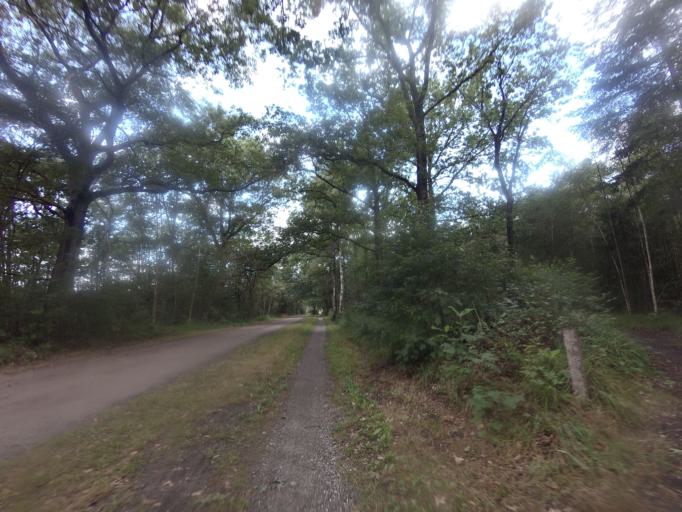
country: NL
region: Overijssel
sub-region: Gemeente Staphorst
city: Staphorst
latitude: 52.6495
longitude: 6.2644
